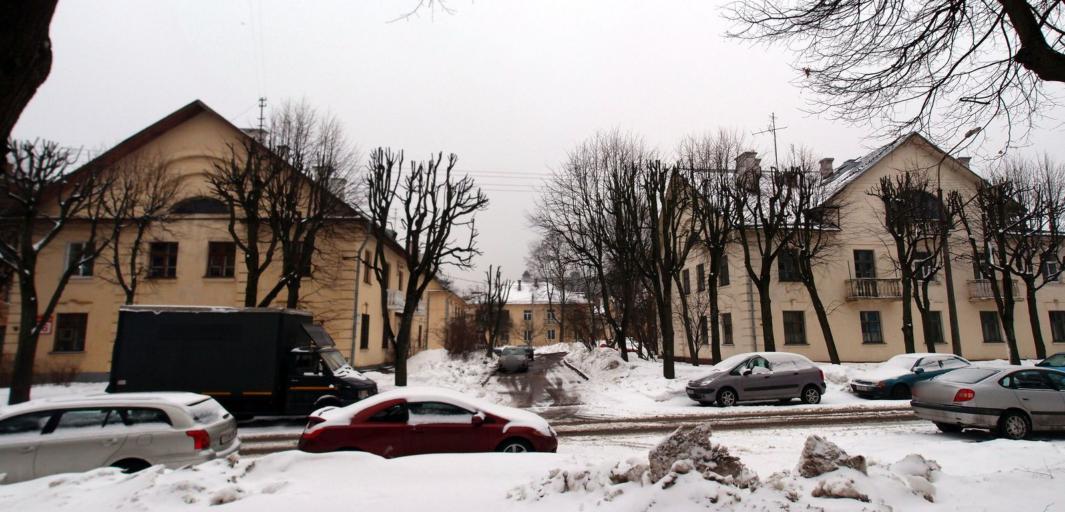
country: BY
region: Minsk
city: Minsk
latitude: 53.9136
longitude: 27.5647
